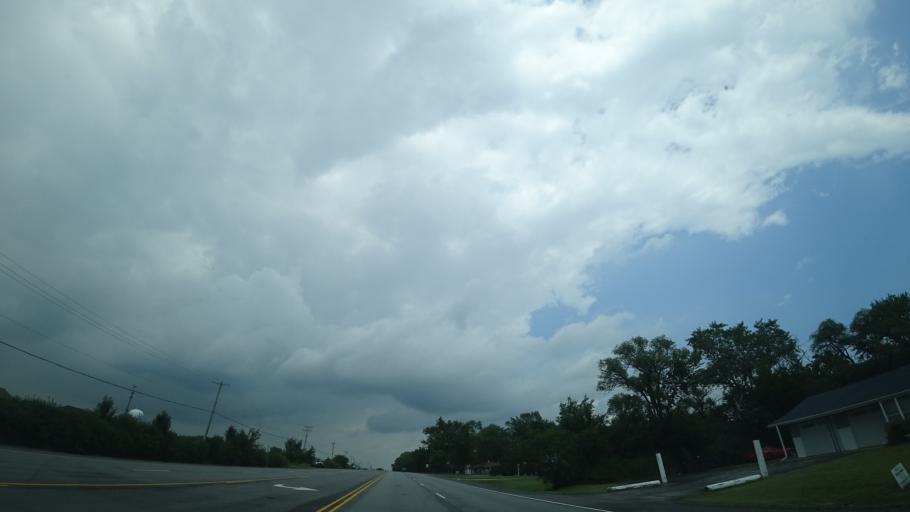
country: US
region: Illinois
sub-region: Cook County
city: Country Club Hills
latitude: 41.5522
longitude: -87.7328
